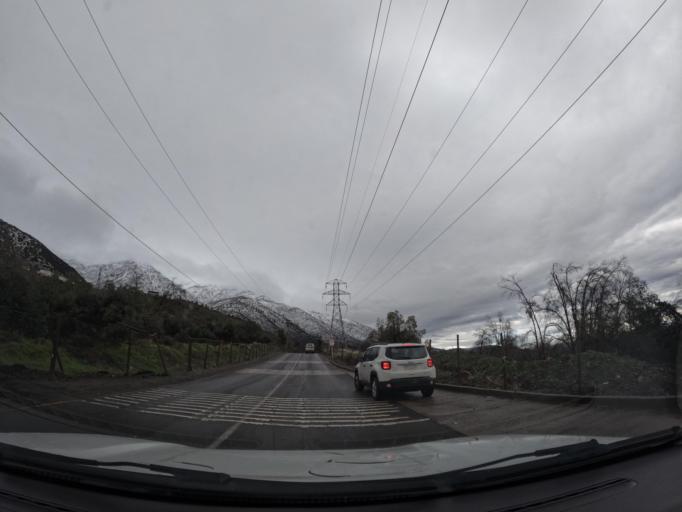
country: CL
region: Santiago Metropolitan
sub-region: Provincia de Santiago
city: Villa Presidente Frei, Nunoa, Santiago, Chile
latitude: -33.4911
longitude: -70.5189
